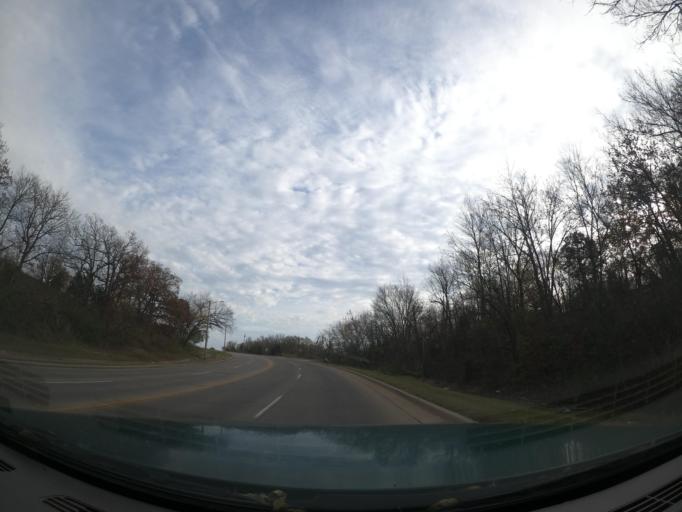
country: US
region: Oklahoma
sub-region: Tulsa County
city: Turley
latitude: 36.2122
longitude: -95.9962
